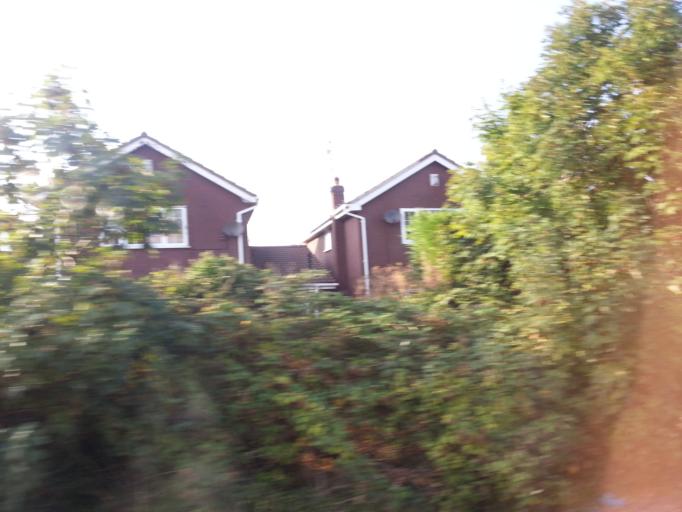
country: GB
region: England
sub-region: Sefton
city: Southport
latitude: 53.6362
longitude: -3.0120
